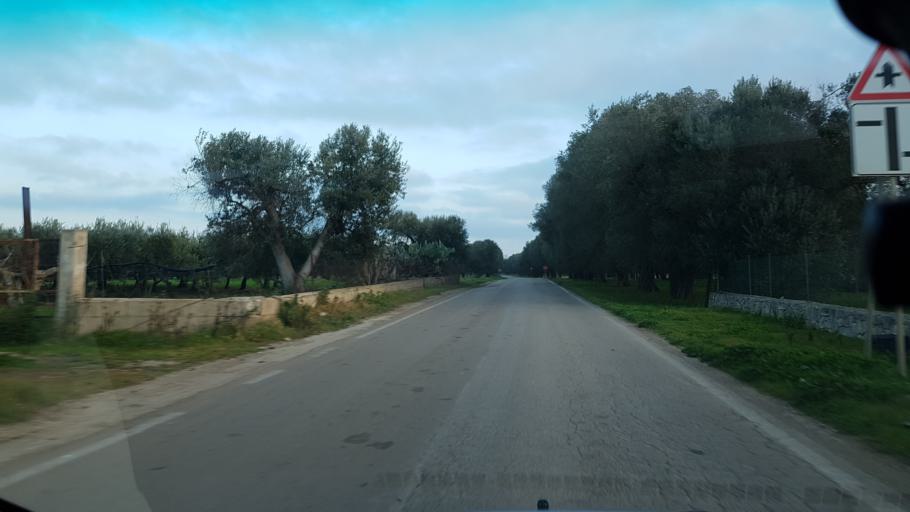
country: IT
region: Apulia
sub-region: Provincia di Brindisi
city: Mesagne
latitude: 40.6129
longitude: 17.7872
